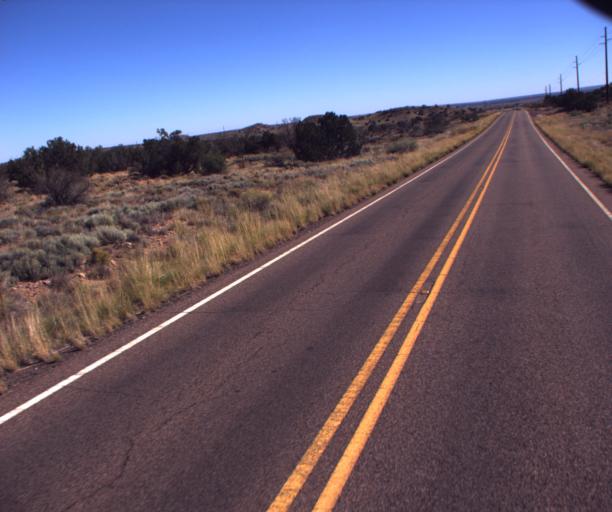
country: US
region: Arizona
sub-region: Navajo County
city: Taylor
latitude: 34.5098
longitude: -110.1740
